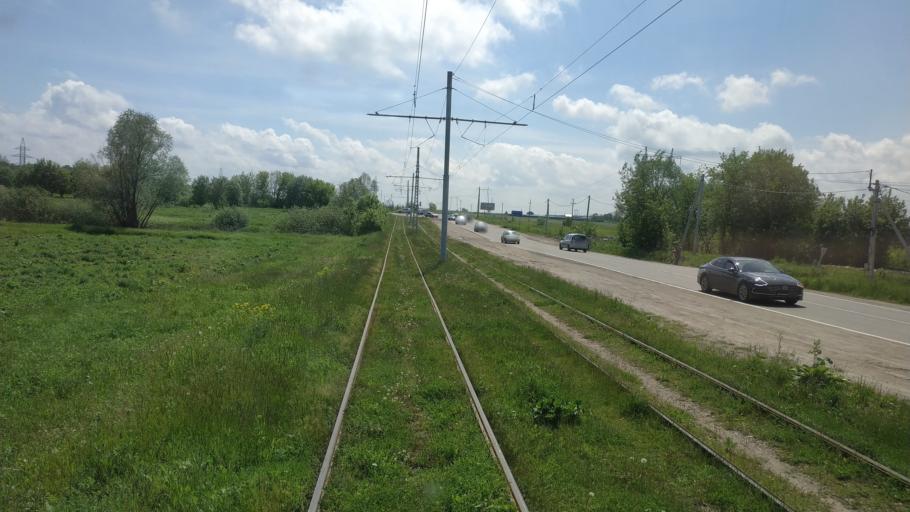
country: RU
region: Moskovskaya
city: Sychevo
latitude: 55.0612
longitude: 38.7265
